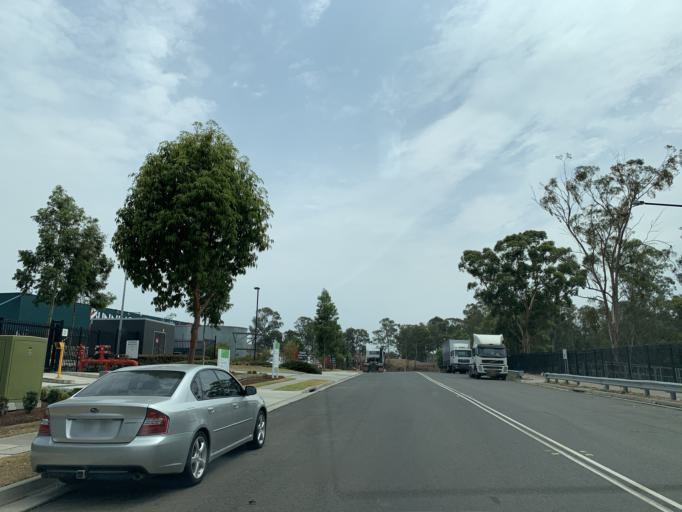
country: AU
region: New South Wales
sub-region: Blacktown
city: Blacktown
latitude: -33.8007
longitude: 150.8998
